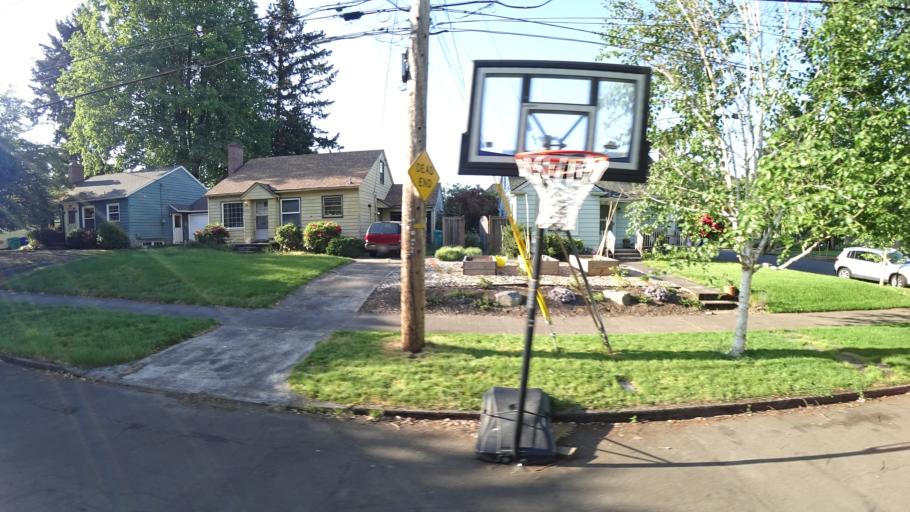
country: US
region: Oregon
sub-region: Multnomah County
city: Portland
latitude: 45.5569
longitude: -122.6879
